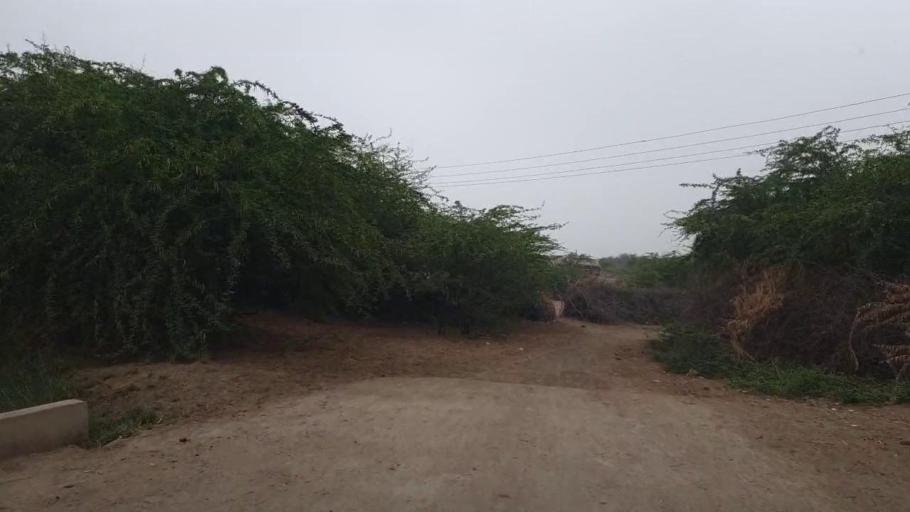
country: PK
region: Sindh
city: Badin
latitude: 24.5959
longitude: 68.6770
